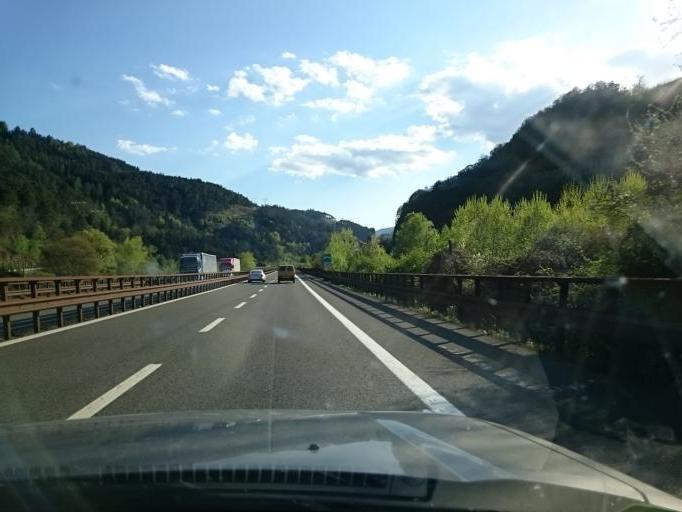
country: IT
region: Trentino-Alto Adige
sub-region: Bolzano
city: Velturno
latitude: 46.6621
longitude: 11.6098
